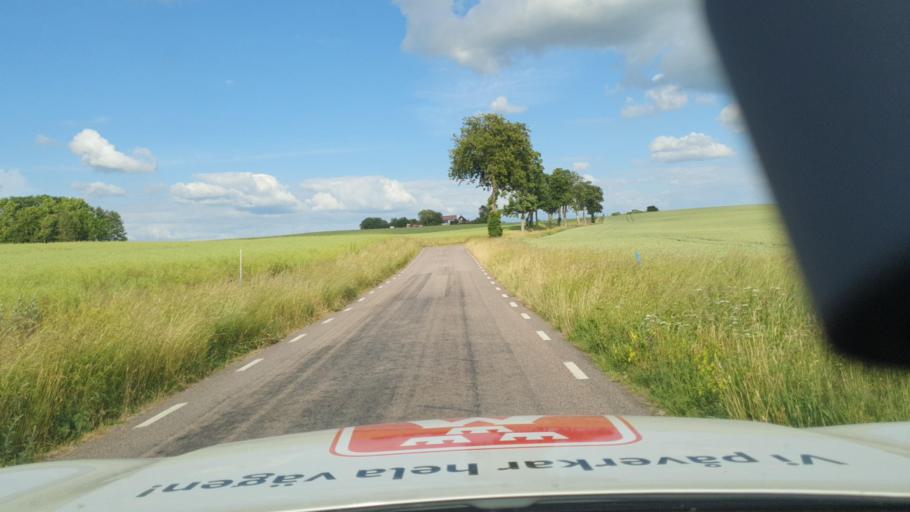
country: SE
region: Skane
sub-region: Skurups Kommun
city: Rydsgard
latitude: 55.4521
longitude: 13.5540
